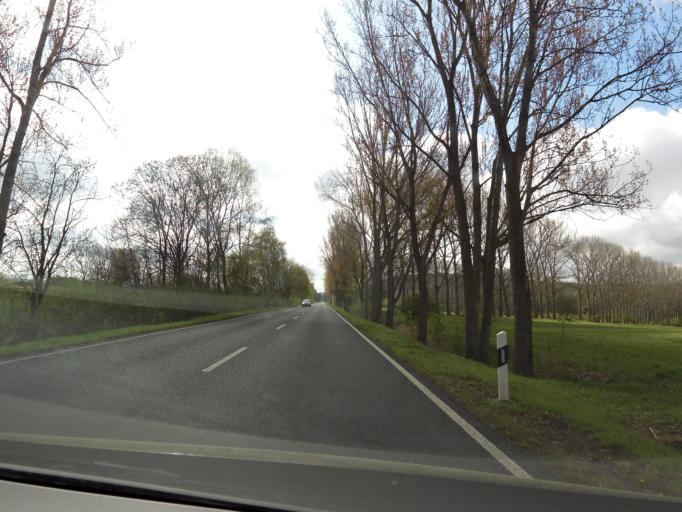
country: DE
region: Thuringia
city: Tuttleben
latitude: 50.9403
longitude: 10.7629
